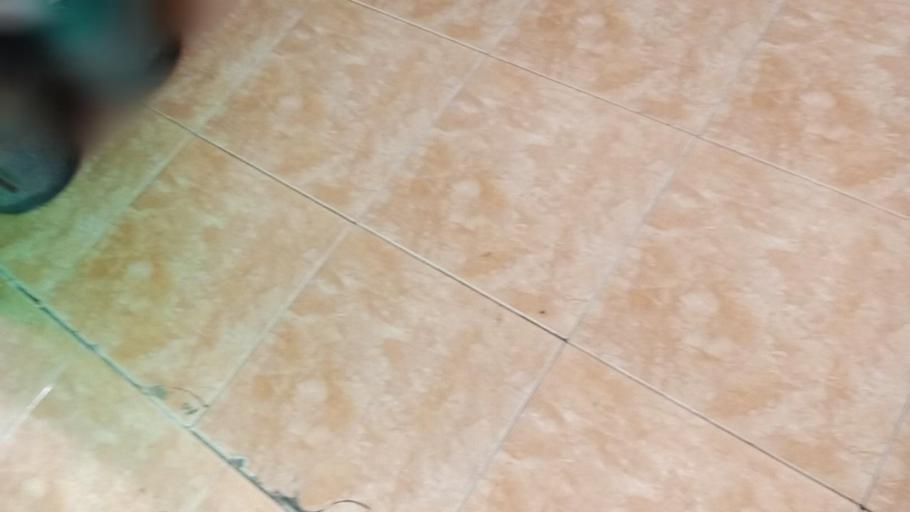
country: ID
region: West Java
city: Parung
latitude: -6.4273
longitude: 106.7362
